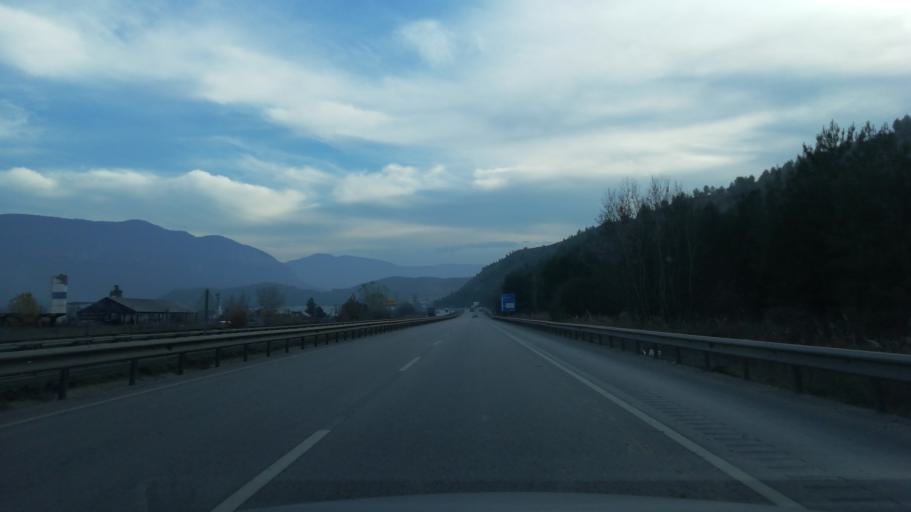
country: TR
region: Karabuk
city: Karabuk
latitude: 41.1426
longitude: 32.6667
